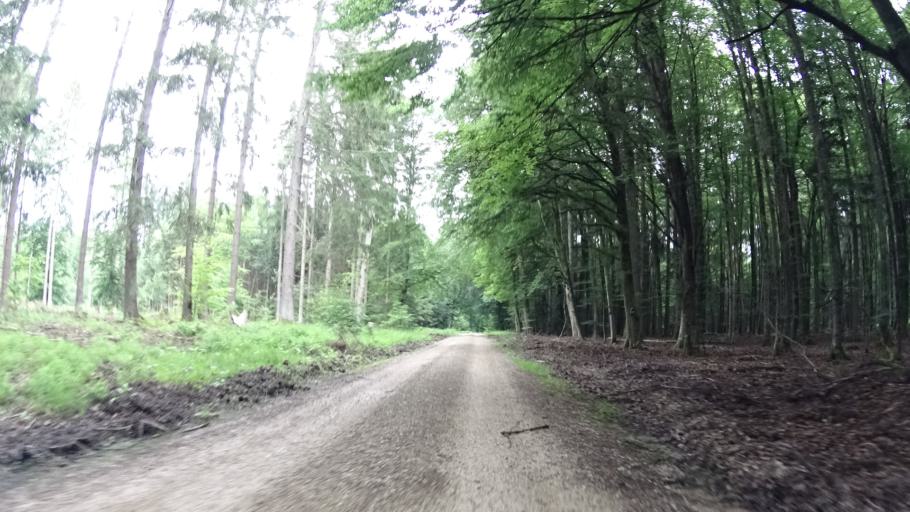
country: DE
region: Bavaria
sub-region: Upper Bavaria
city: Stammham
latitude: 48.8824
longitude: 11.5233
